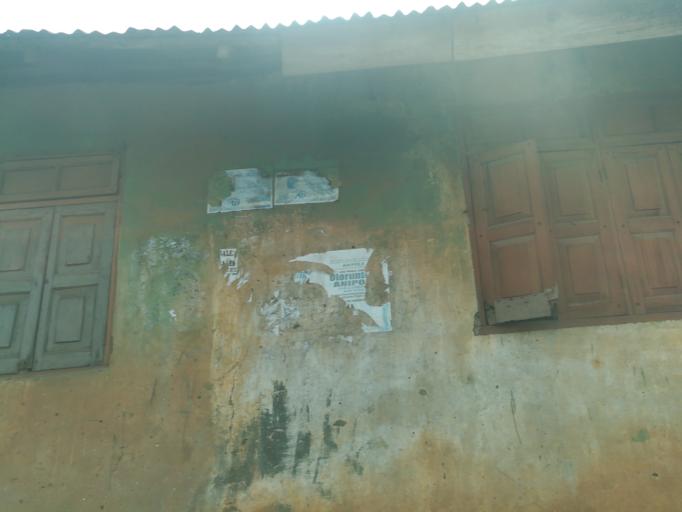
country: NG
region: Lagos
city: Ikorodu
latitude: 6.6121
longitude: 3.5074
